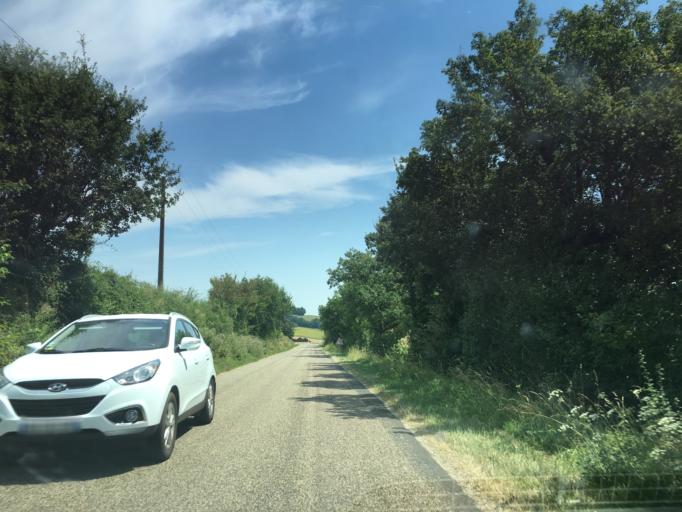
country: FR
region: Midi-Pyrenees
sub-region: Departement du Gers
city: Jegun
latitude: 43.8094
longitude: 0.5063
